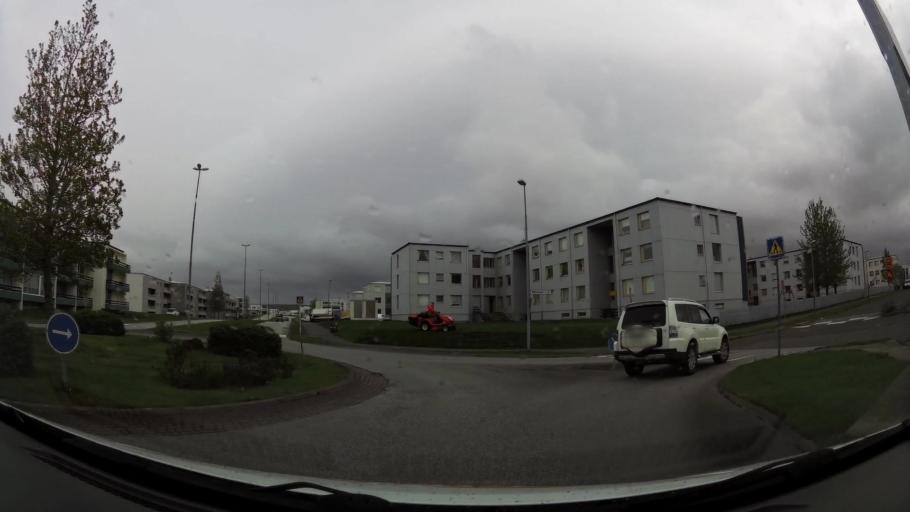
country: IS
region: Capital Region
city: Hafnarfjoerdur
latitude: 64.0791
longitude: -21.9564
